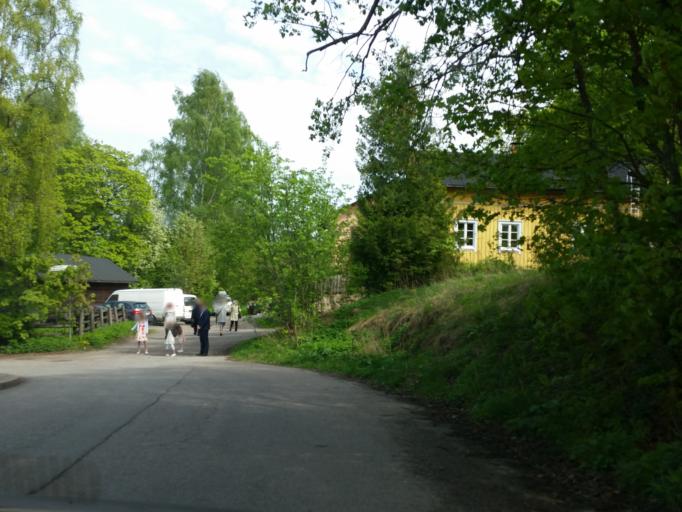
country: FI
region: Uusimaa
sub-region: Helsinki
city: Helsinki
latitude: 60.2431
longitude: 24.9638
